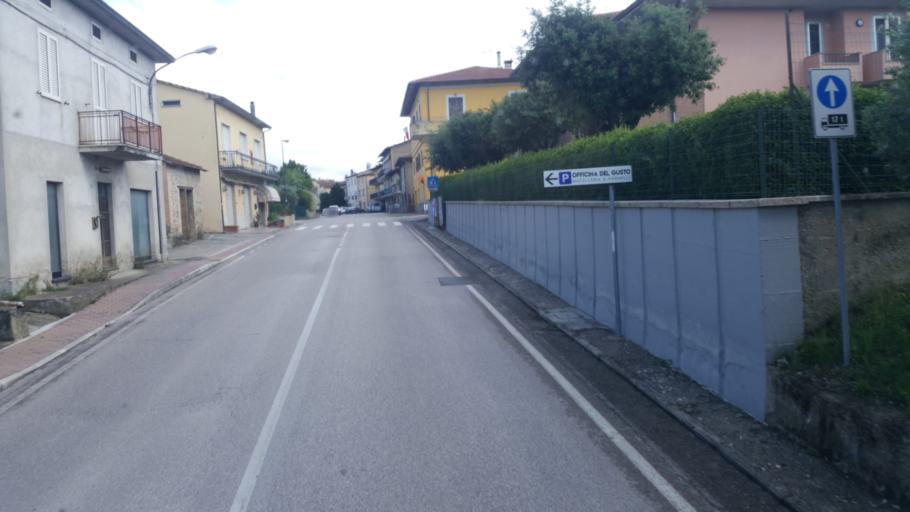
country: IT
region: Umbria
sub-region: Provincia di Perugia
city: Torgiano
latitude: 43.0256
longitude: 12.4454
